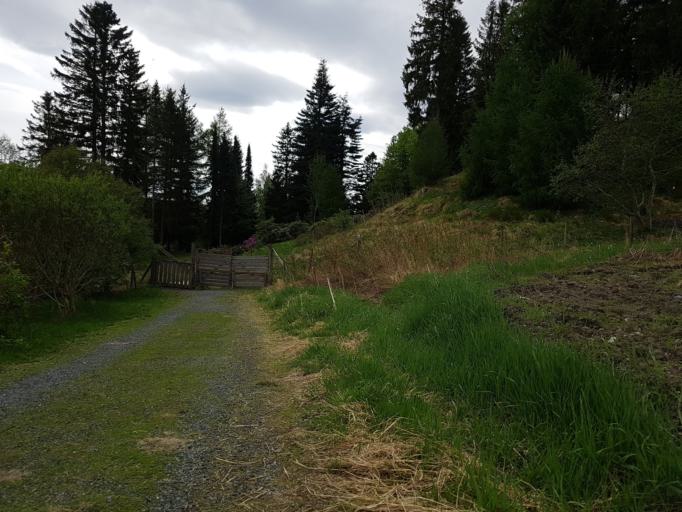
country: NO
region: Nord-Trondelag
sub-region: Levanger
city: Levanger
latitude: 63.7432
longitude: 11.2710
